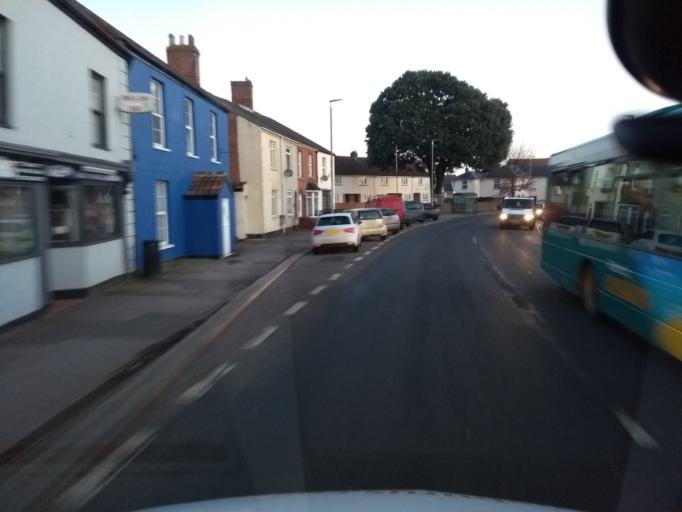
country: GB
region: England
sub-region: Somerset
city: North Petherton
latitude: 51.0912
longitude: -3.0172
